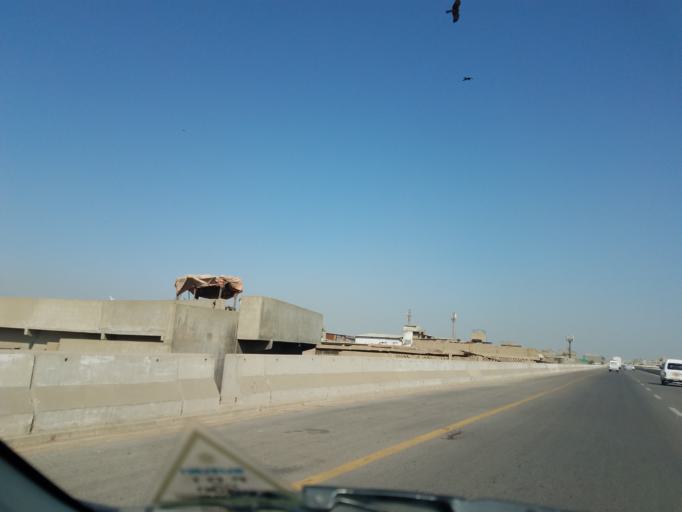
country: PK
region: Sindh
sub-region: Karachi District
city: Karachi
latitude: 24.8821
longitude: 66.9989
